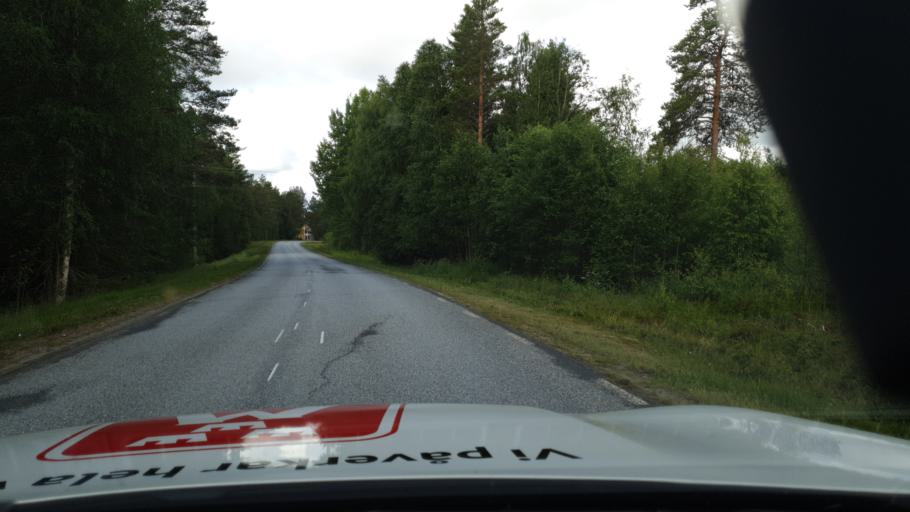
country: SE
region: Vaesterbotten
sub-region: Umea Kommun
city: Hoernefors
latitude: 63.6812
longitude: 20.0337
